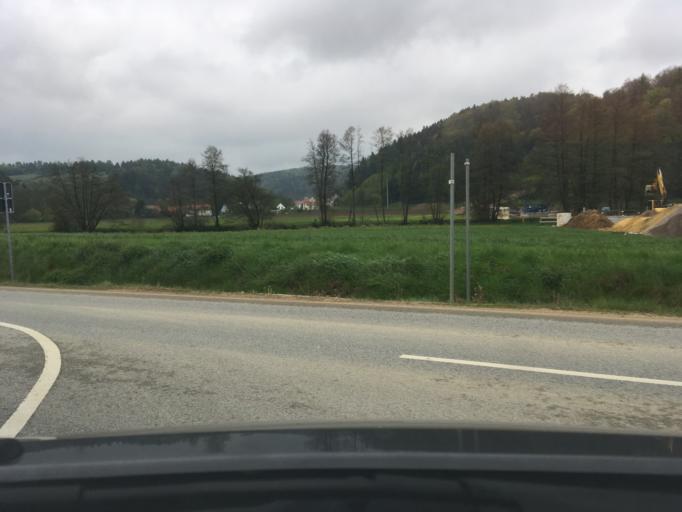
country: DE
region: Bavaria
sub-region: Upper Palatinate
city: Kallmunz
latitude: 49.1781
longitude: 11.9470
